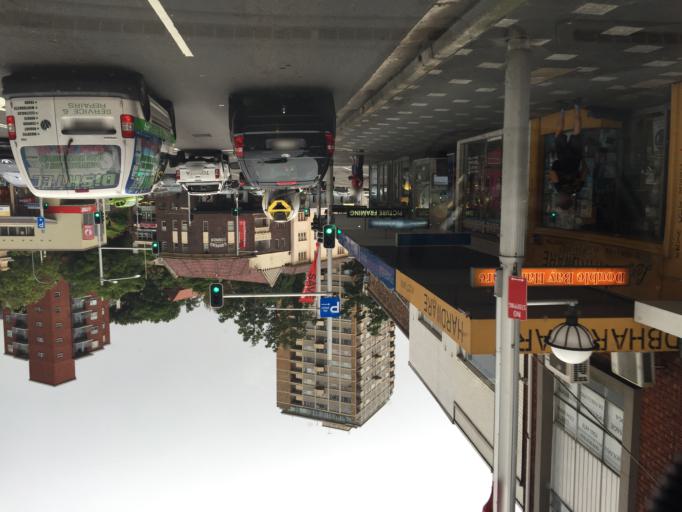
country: AU
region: New South Wales
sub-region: Woollahra
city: Bellevue Hill
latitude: -33.8773
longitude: 151.2442
